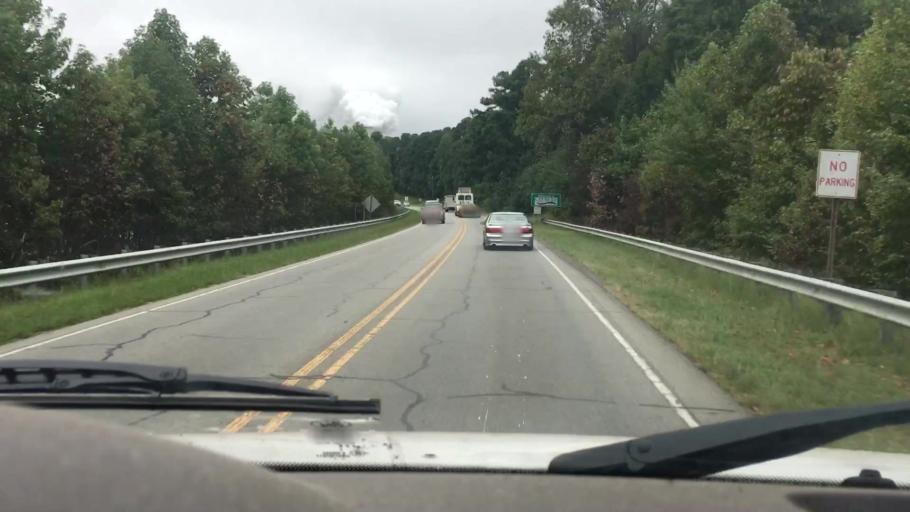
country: US
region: North Carolina
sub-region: Catawba County
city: Lake Norman of Catawba
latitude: 35.6040
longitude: -80.9476
